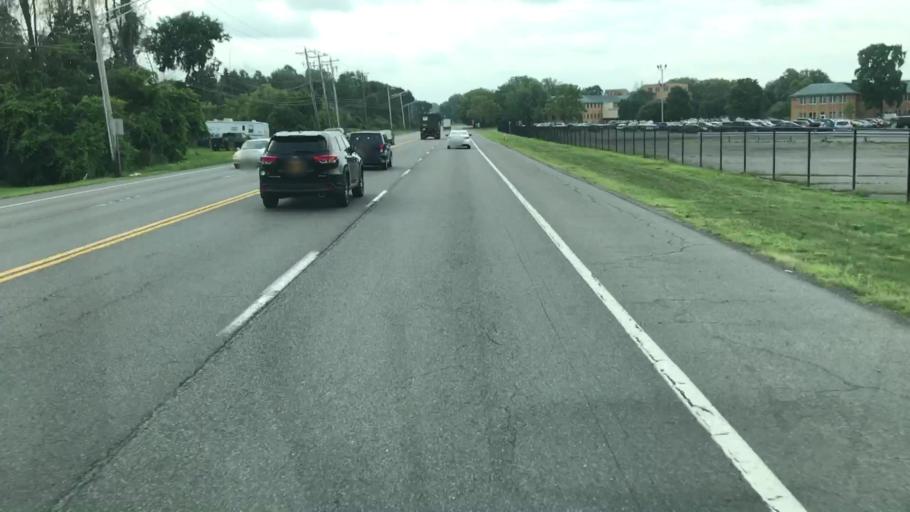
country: US
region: New York
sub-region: Onondaga County
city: Galeville
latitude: 43.1134
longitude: -76.1848
